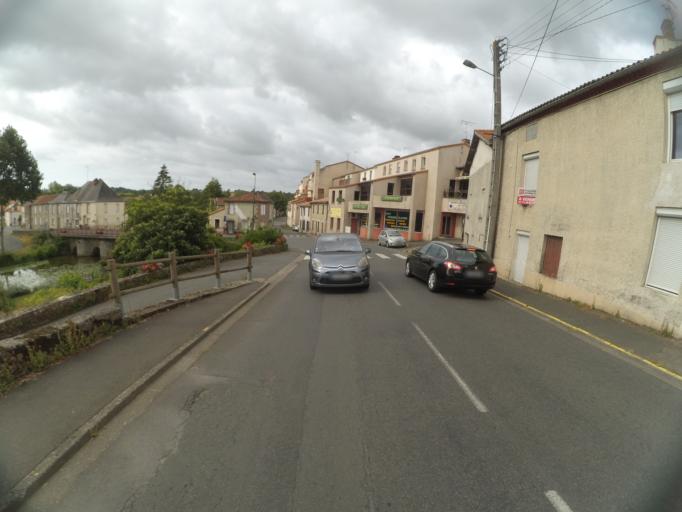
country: FR
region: Pays de la Loire
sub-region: Departement de Maine-et-Loire
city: Montfaucon-Montigne
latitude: 47.0988
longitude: -1.1270
